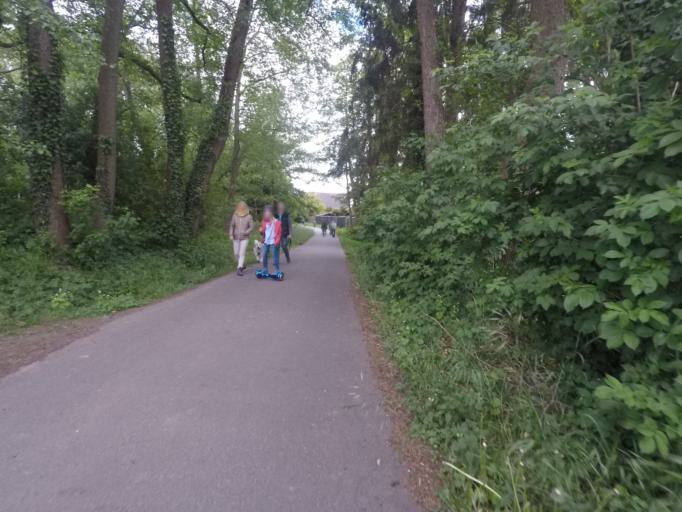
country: DE
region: North Rhine-Westphalia
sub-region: Regierungsbezirk Detmold
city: Herford
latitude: 52.1120
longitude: 8.7098
